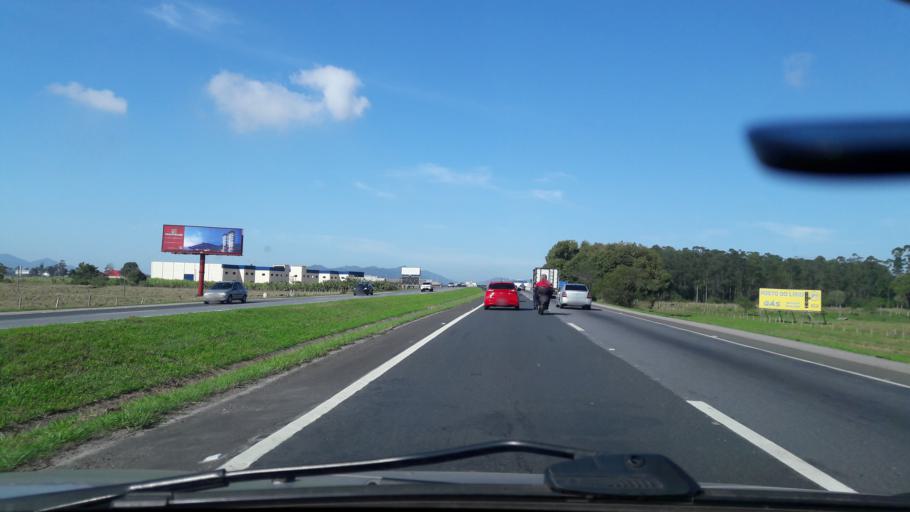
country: BR
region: Santa Catarina
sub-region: Tijucas
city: Tijucas
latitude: -27.2091
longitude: -48.6203
